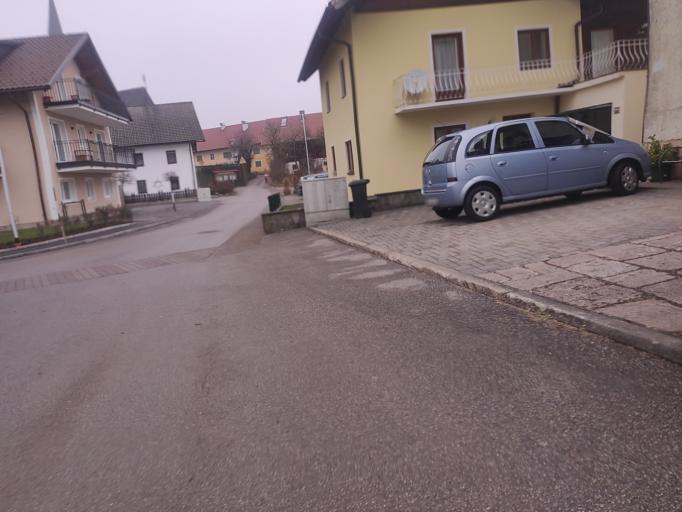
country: AT
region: Salzburg
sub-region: Politischer Bezirk Salzburg-Umgebung
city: Schleedorf
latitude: 47.9523
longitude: 13.1532
